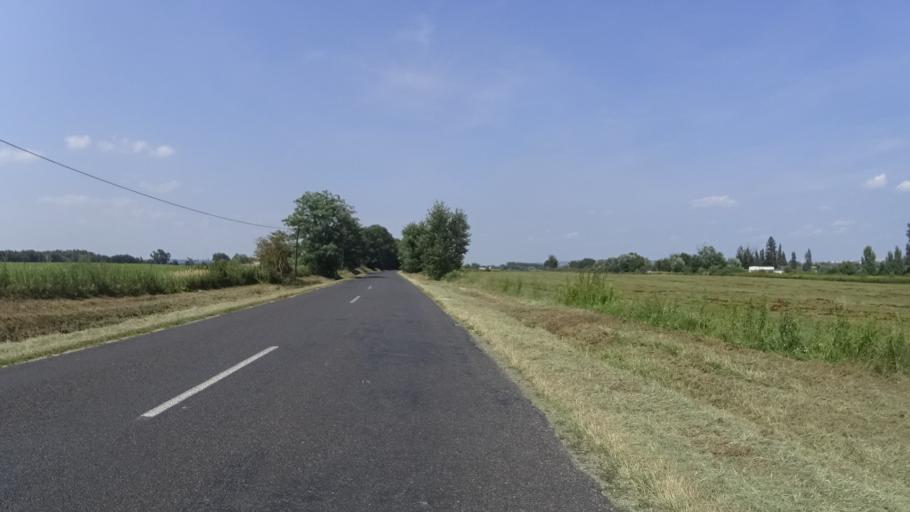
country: HU
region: Zala
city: Nagykanizsa
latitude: 46.4298
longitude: 16.9533
